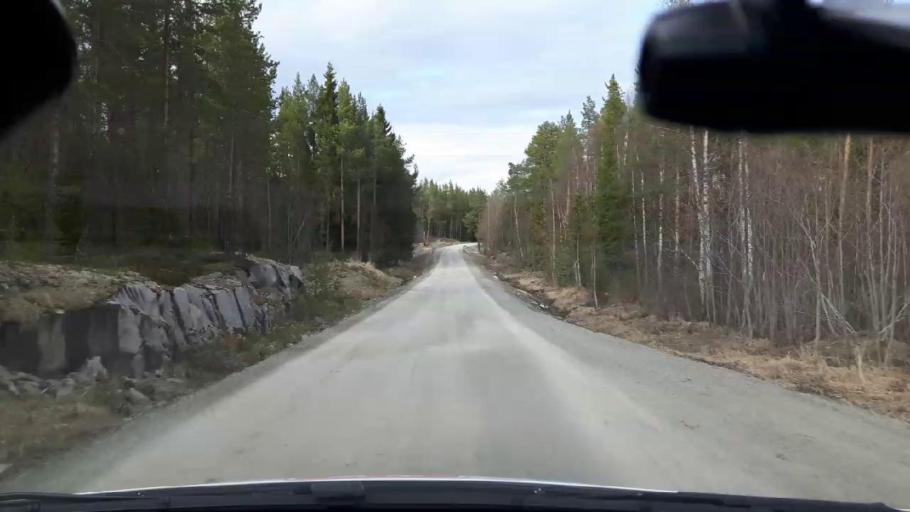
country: SE
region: Jaemtland
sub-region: OEstersunds Kommun
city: Brunflo
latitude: 62.9317
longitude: 14.6494
